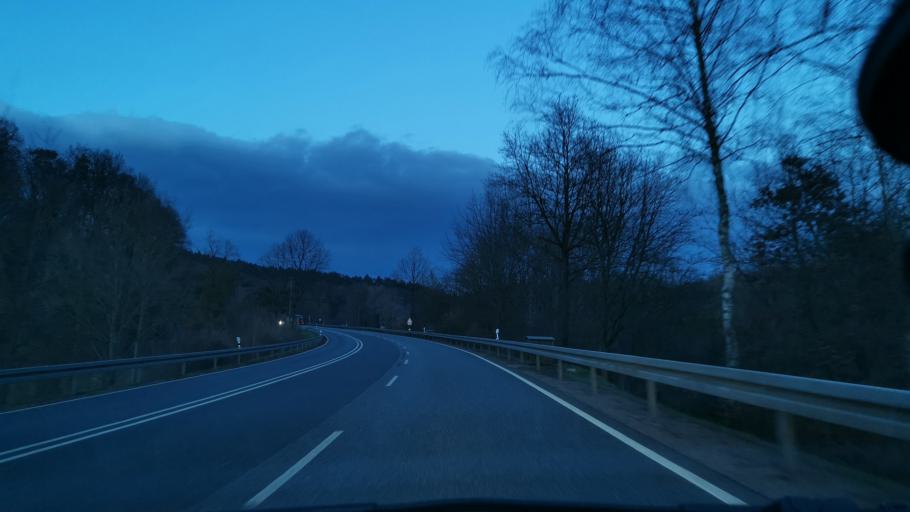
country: DE
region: Hesse
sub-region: Regierungsbezirk Kassel
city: Cornberg
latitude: 51.0235
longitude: 9.8347
